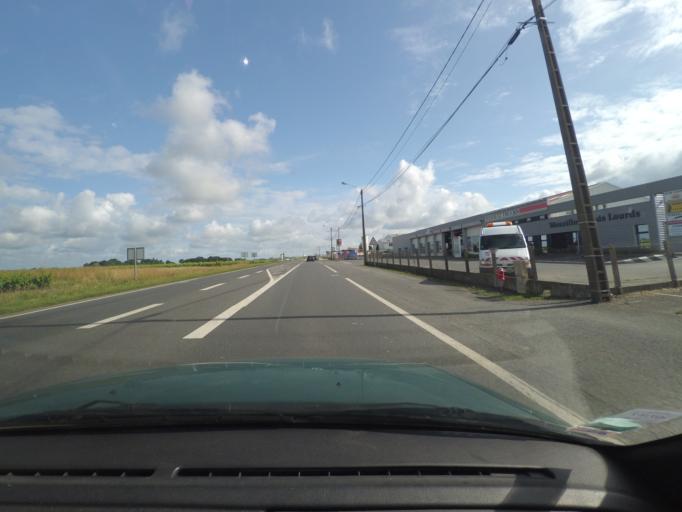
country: FR
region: Pays de la Loire
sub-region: Departement de la Loire-Atlantique
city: Mouzillon
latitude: 47.1237
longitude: -1.2826
